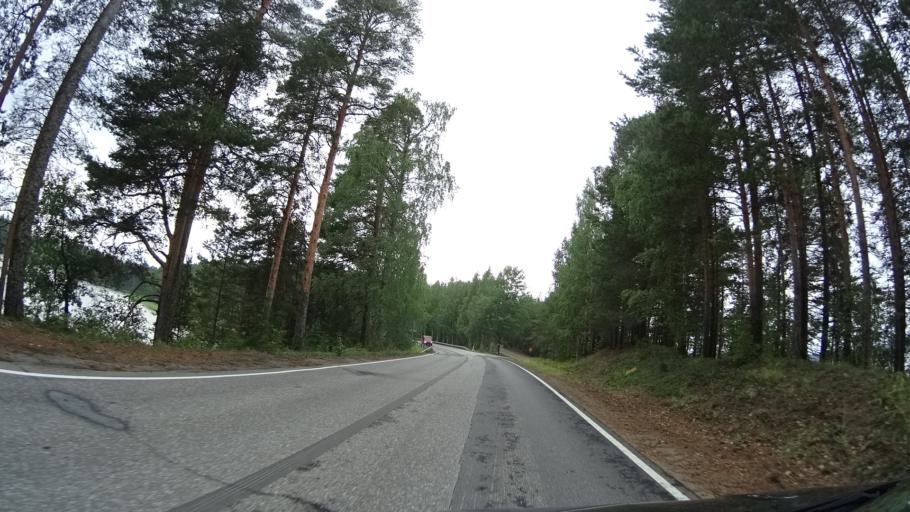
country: FI
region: Southern Savonia
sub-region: Savonlinna
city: Punkaharju
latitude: 61.7574
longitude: 29.4069
